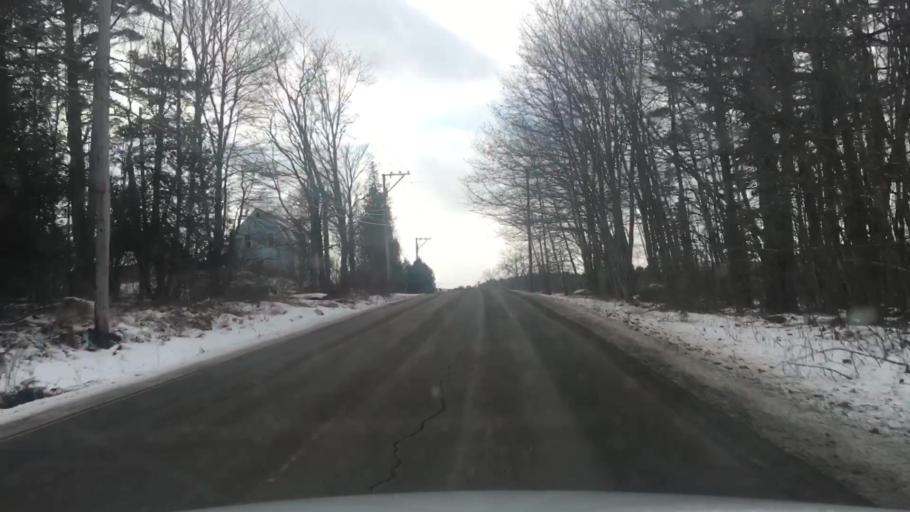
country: US
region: Maine
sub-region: Knox County
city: Hope
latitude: 44.2900
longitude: -69.0938
